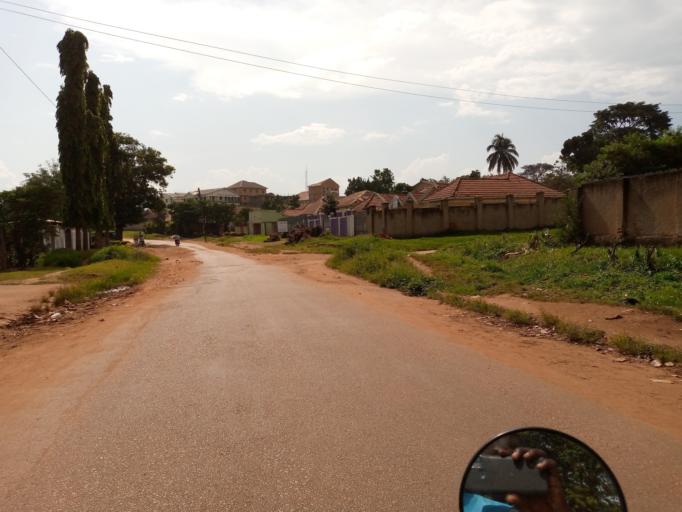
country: UG
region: Eastern Region
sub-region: Mbale District
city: Mbale
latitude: 1.0766
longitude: 34.1717
